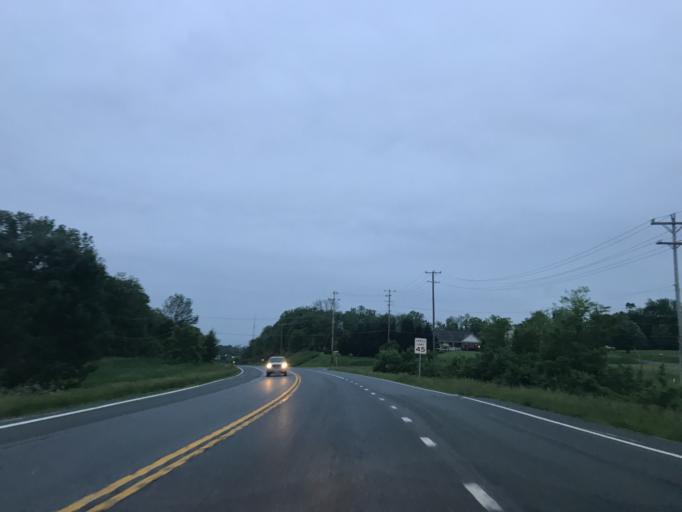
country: US
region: Maryland
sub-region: Frederick County
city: Linganore
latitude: 39.3926
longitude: -77.2617
